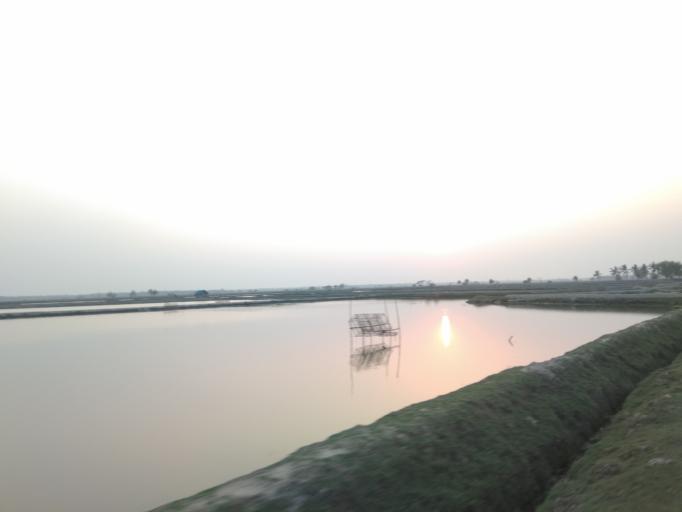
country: IN
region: West Bengal
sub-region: North 24 Parganas
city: Taki
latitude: 22.4557
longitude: 89.0760
